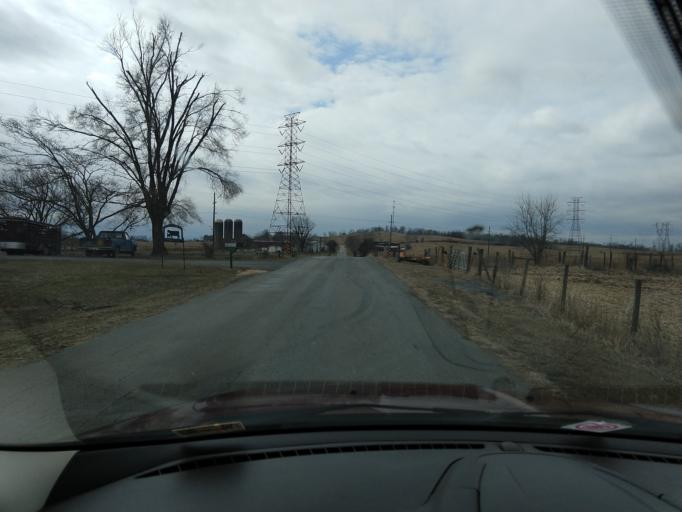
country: US
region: Virginia
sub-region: Augusta County
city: Dooms
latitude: 38.1202
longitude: -78.9029
